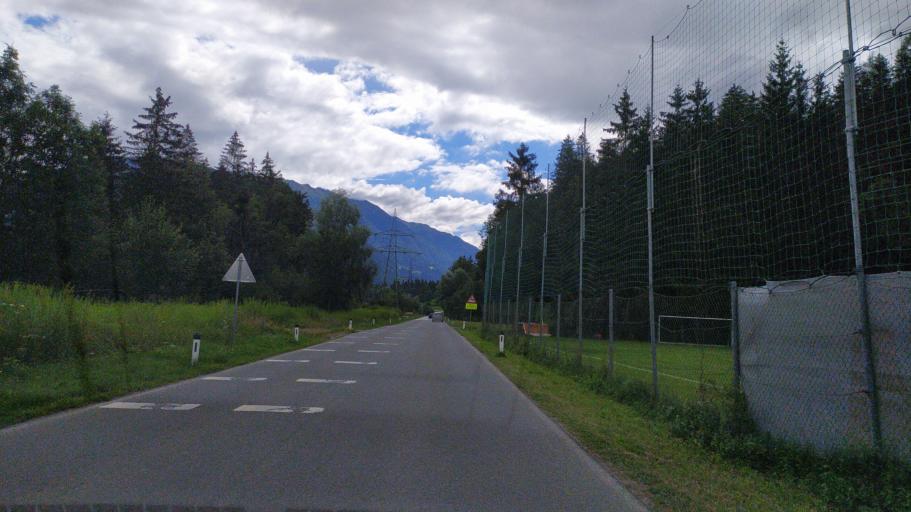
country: AT
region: Tyrol
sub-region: Politischer Bezirk Lienz
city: Tristach
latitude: 46.8148
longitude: 12.8022
